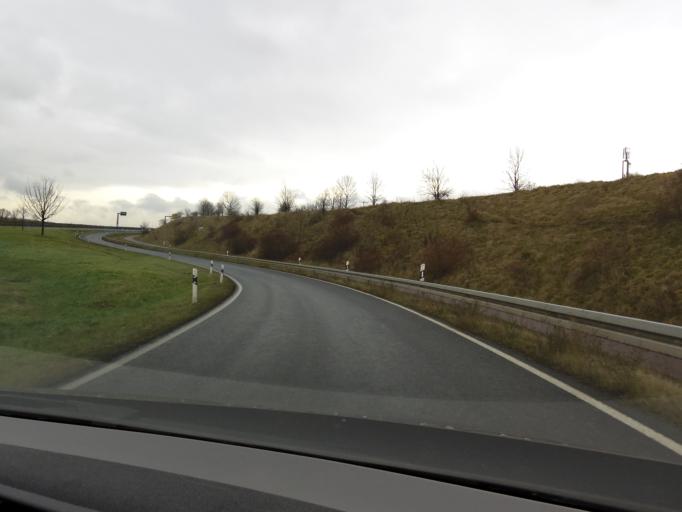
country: DE
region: Saxony-Anhalt
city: Burgwerben
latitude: 51.2132
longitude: 11.9960
